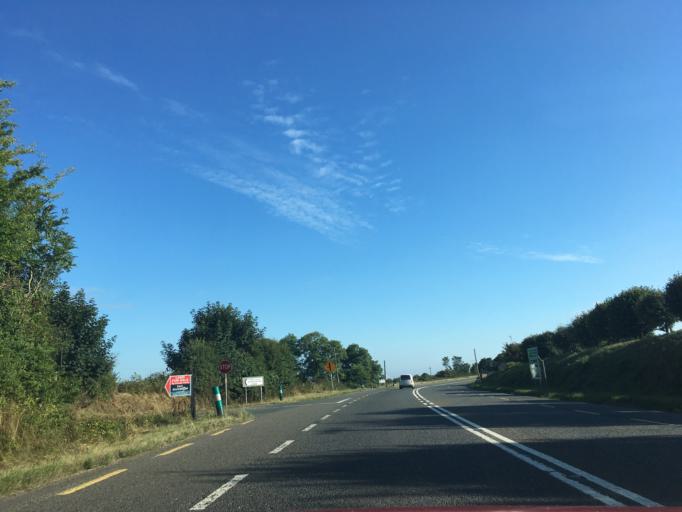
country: IE
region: Munster
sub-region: Waterford
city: Waterford
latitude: 52.3098
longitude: -7.0495
